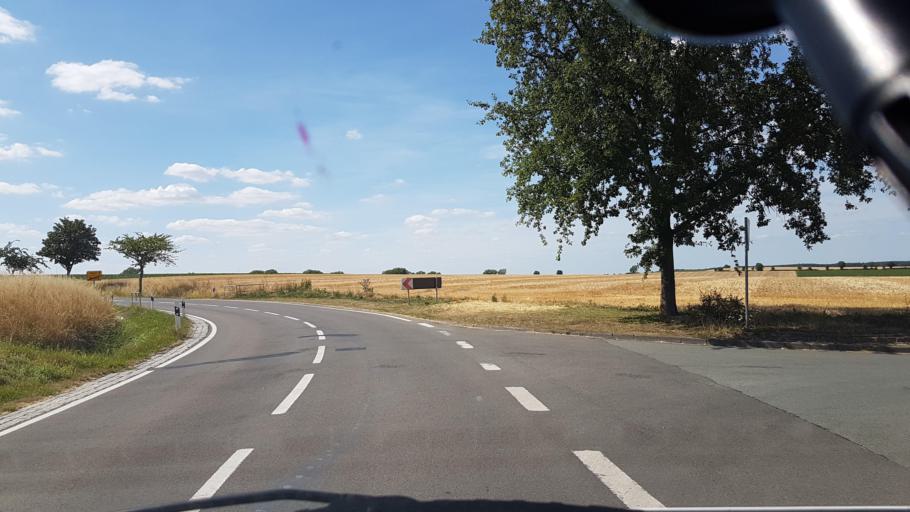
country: DE
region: Lower Saxony
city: Warberg
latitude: 52.1812
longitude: 10.9147
